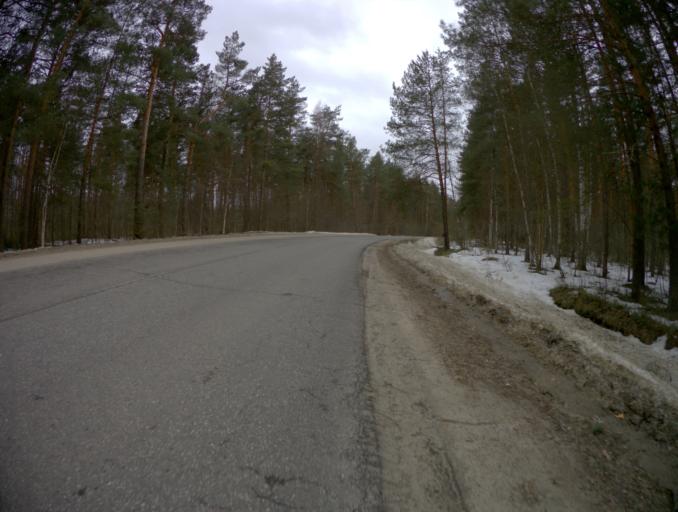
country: RU
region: Vladimir
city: Bogolyubovo
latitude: 56.1480
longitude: 40.5269
